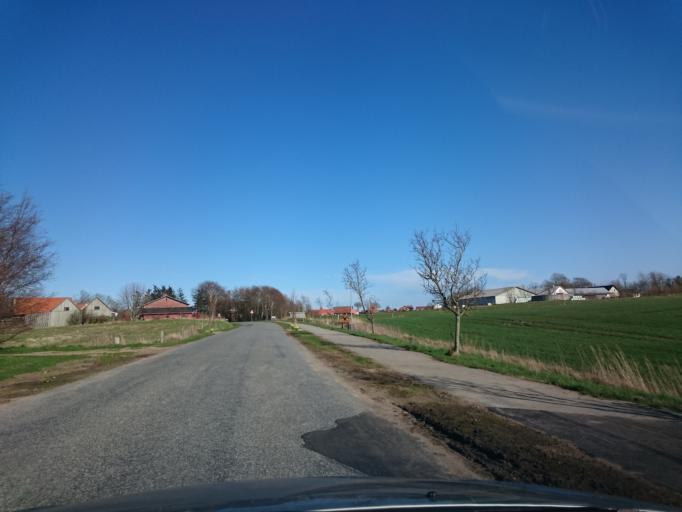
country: DK
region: North Denmark
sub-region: Hjorring Kommune
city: Sindal
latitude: 57.5658
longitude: 10.1022
